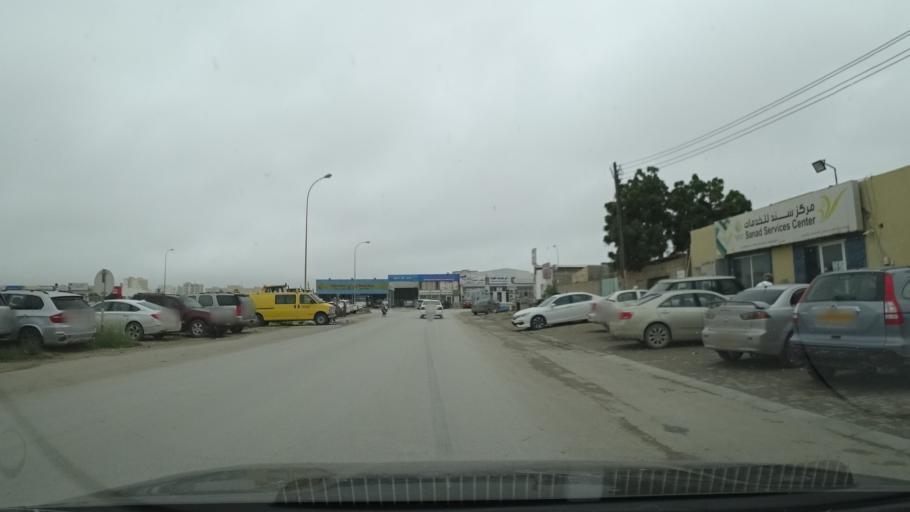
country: OM
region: Zufar
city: Salalah
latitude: 17.0179
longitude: 54.0417
